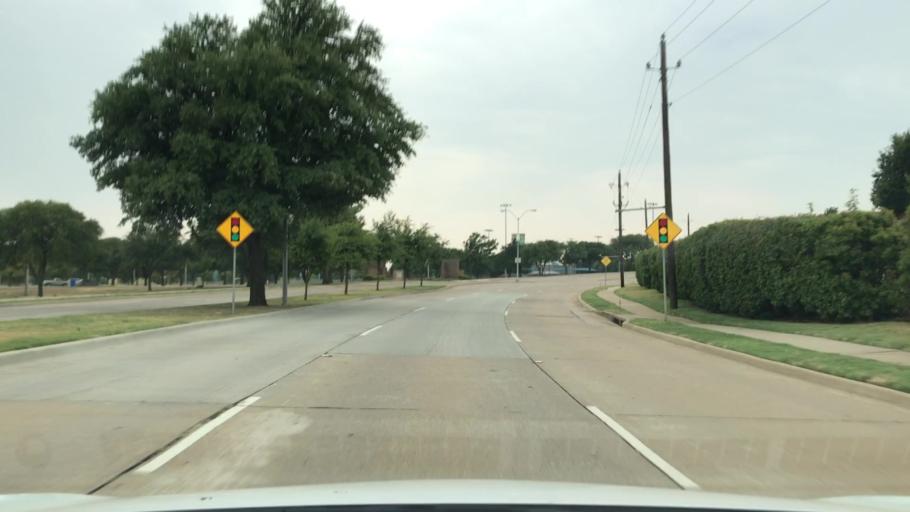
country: US
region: Texas
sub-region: Dallas County
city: Carrollton
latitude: 32.9695
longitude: -96.8957
